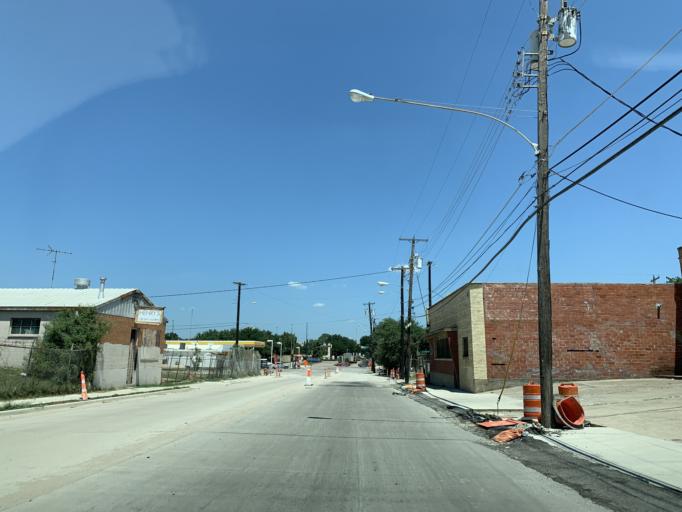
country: US
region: Texas
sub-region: Dallas County
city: Dallas
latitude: 32.7765
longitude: -96.7663
